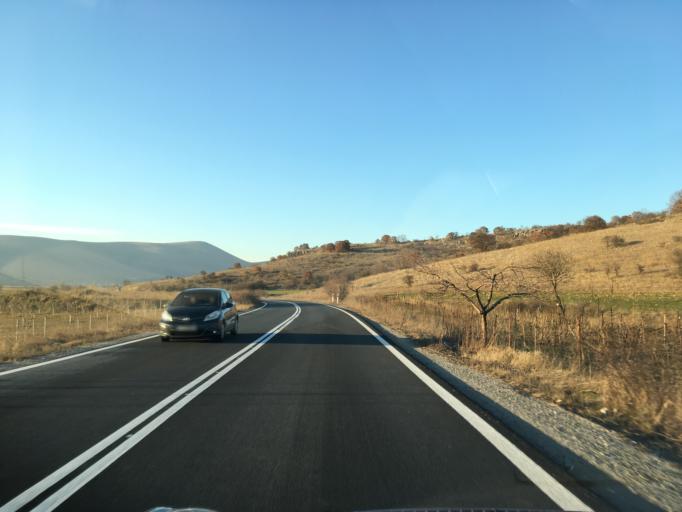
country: GR
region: West Macedonia
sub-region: Nomos Kozanis
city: Kozani
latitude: 40.3068
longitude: 21.7354
